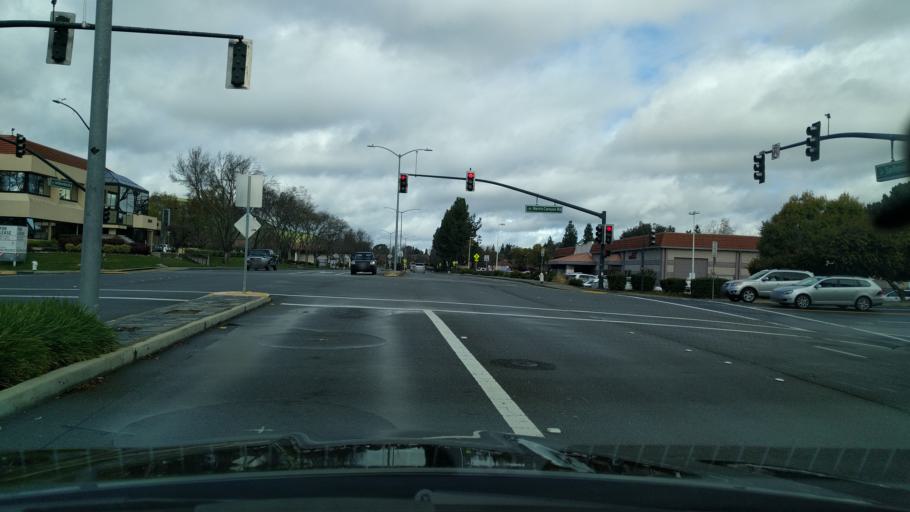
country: US
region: California
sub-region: Contra Costa County
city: San Ramon
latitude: 37.7709
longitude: -121.9733
